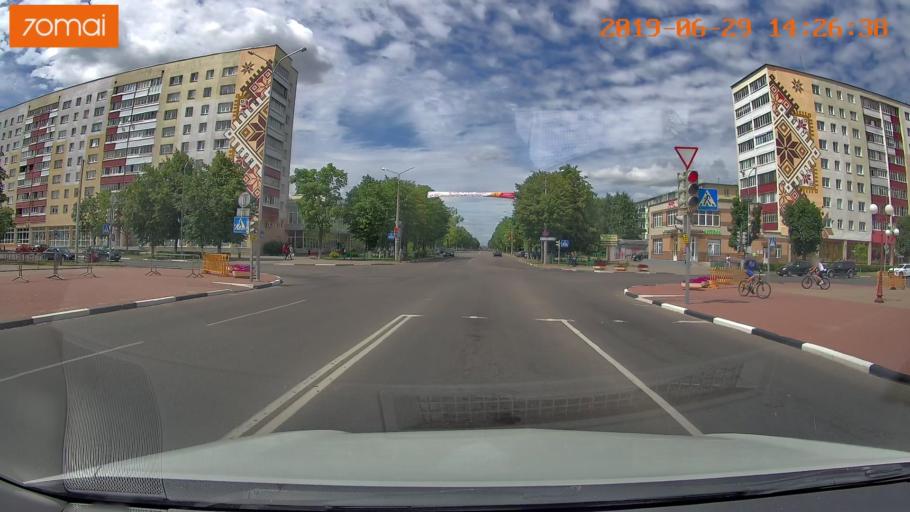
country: BY
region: Minsk
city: Salihorsk
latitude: 52.7838
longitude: 27.5409
